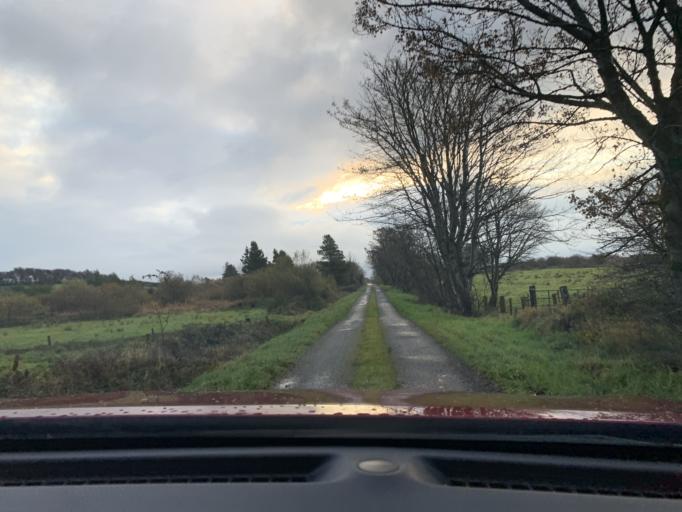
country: IE
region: Connaught
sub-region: Sligo
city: Ballymote
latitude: 54.0332
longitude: -8.5336
